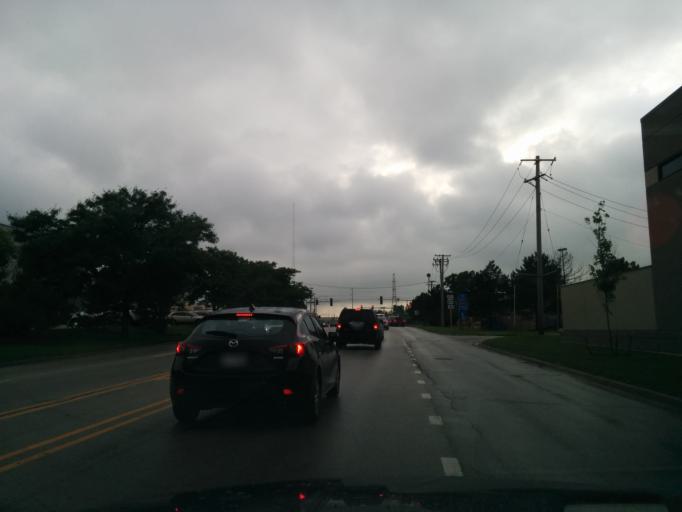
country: US
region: Illinois
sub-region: Cook County
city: Berkeley
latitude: 41.9044
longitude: -87.9113
